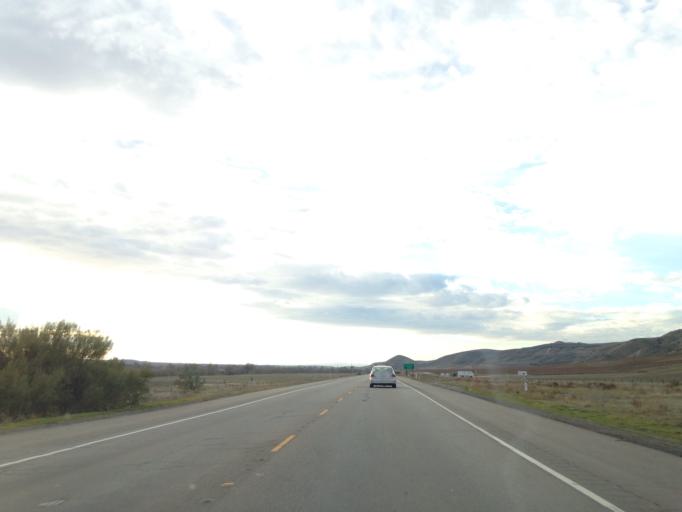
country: US
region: California
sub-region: San Luis Obispo County
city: Shandon
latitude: 35.6624
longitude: -120.3722
